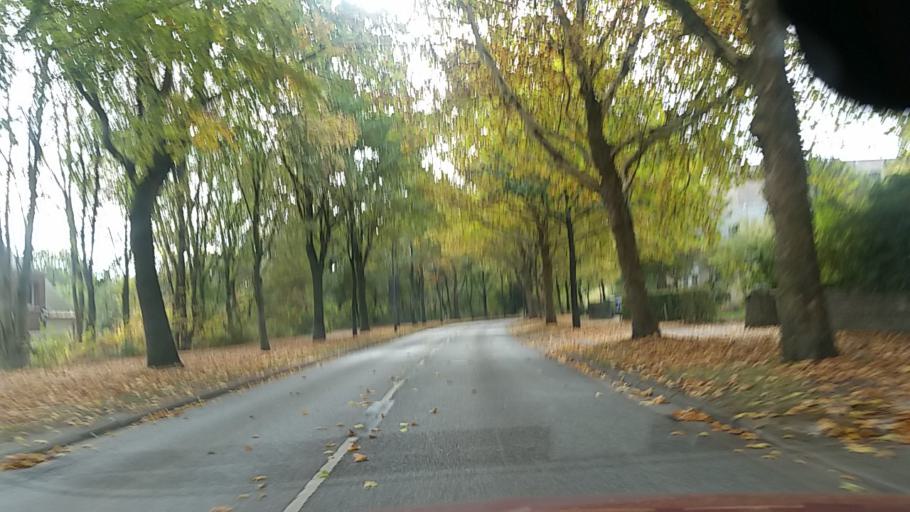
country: DE
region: Hamburg
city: Hummelsbuettel
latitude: 53.6450
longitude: 10.0420
